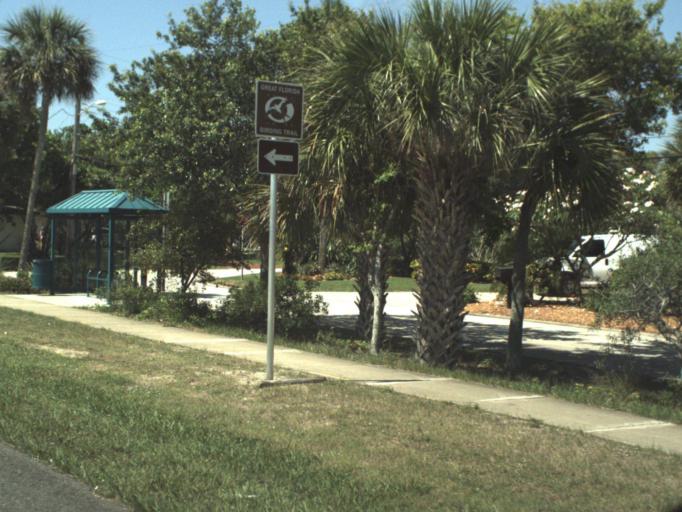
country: US
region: Florida
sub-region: Brevard County
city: Cocoa Beach
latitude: 28.3374
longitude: -80.6104
